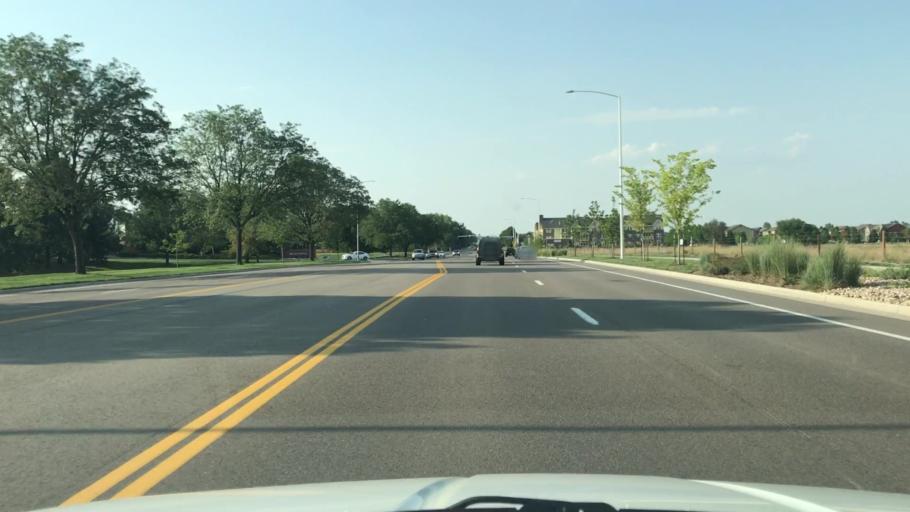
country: US
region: Colorado
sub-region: Broomfield County
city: Broomfield
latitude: 39.9181
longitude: -105.0343
